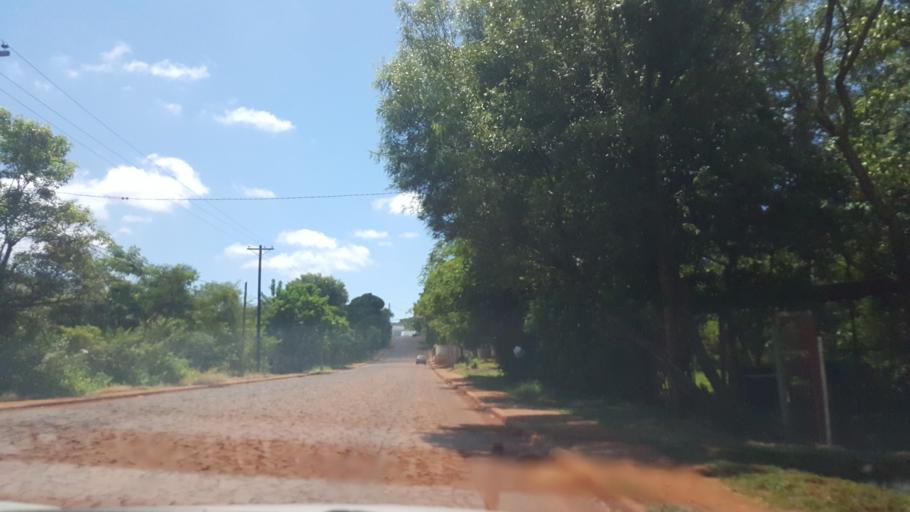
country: AR
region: Misiones
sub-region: Departamento de Capital
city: Posadas
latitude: -27.4023
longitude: -55.9438
